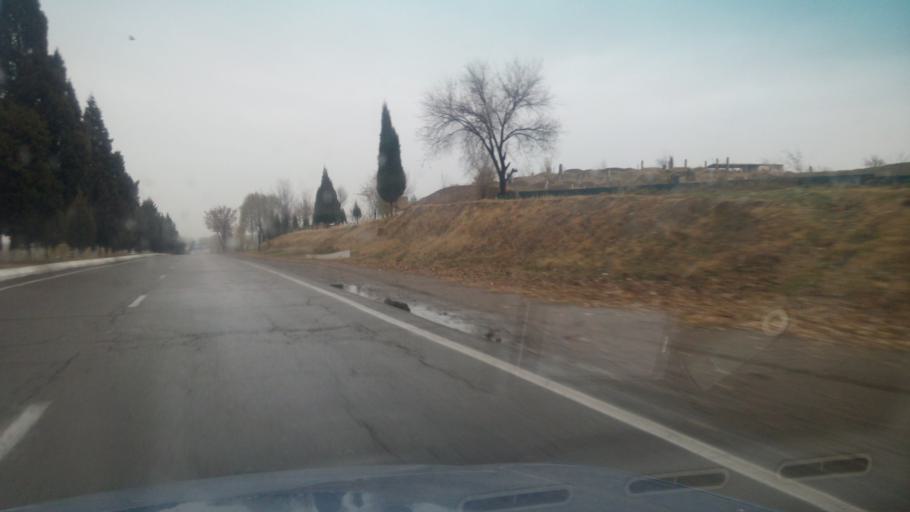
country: UZ
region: Toshkent
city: Amir Timur
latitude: 41.0447
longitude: 68.8873
